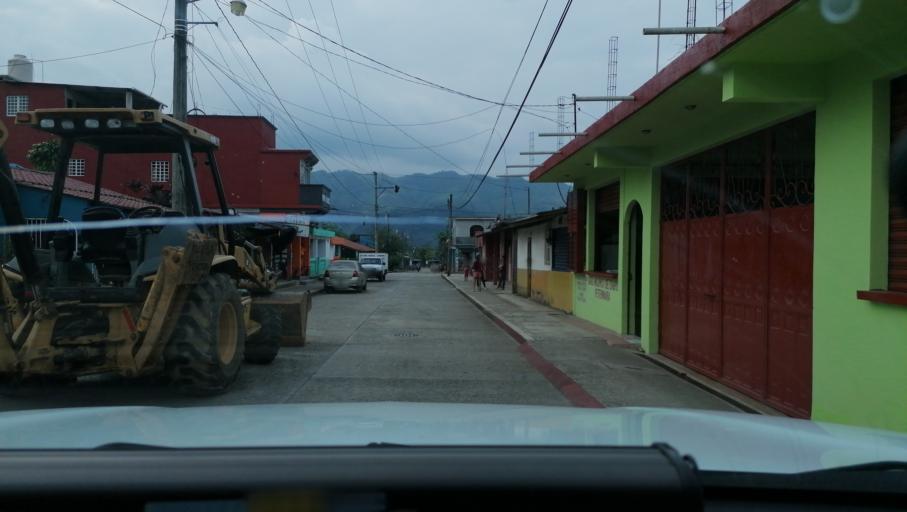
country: MX
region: Chiapas
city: Ixtacomitan
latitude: 17.3412
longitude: -93.1310
